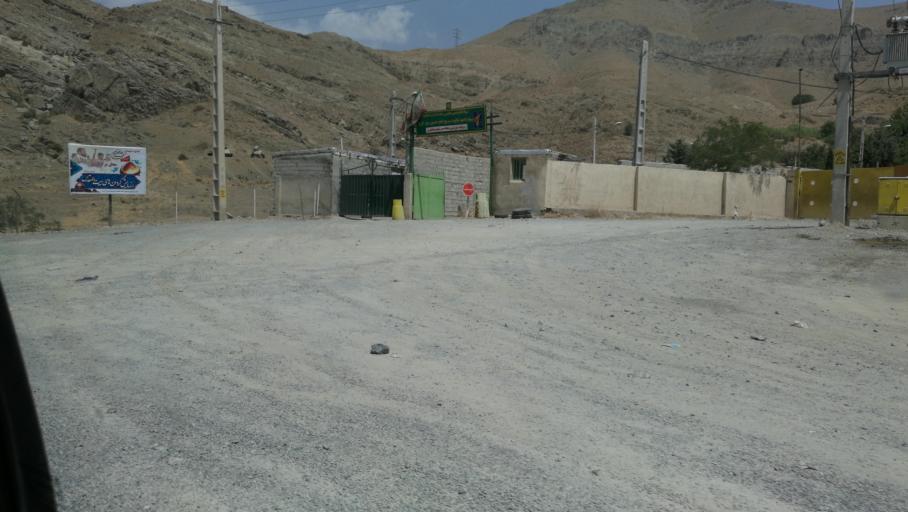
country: IR
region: Alborz
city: Karaj
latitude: 35.8265
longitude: 51.0418
